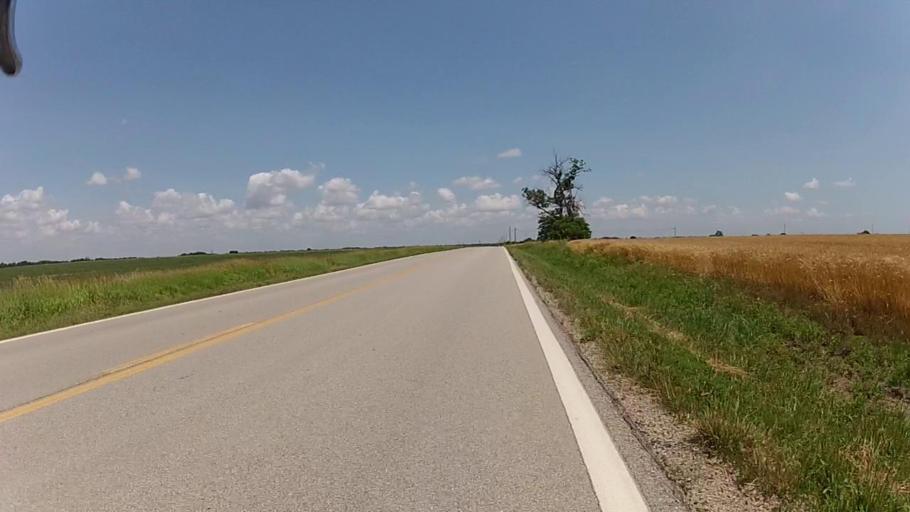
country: US
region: Kansas
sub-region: Labette County
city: Altamont
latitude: 37.1926
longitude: -95.4342
